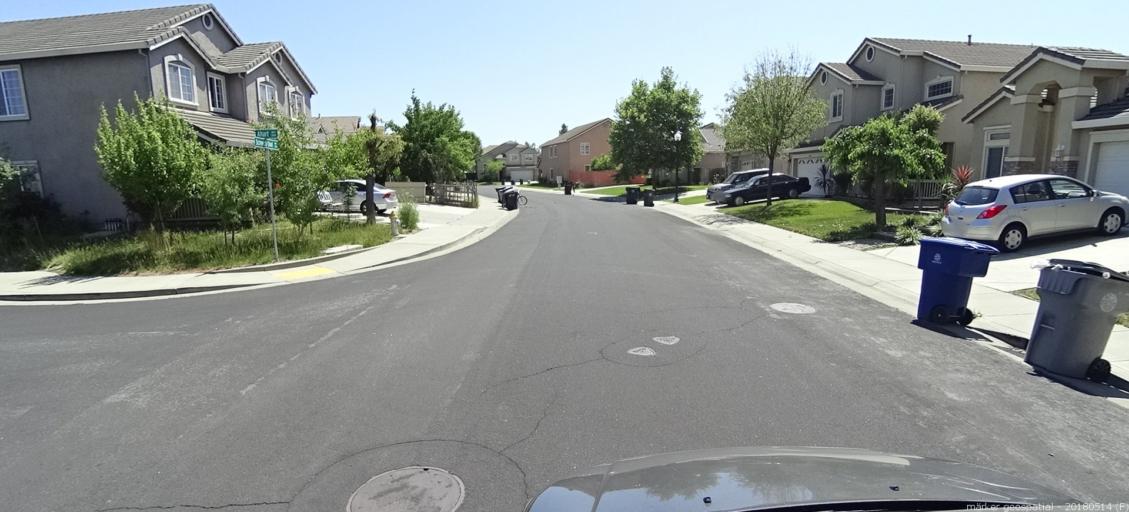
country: US
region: California
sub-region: Yolo County
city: West Sacramento
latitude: 38.6323
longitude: -121.5274
